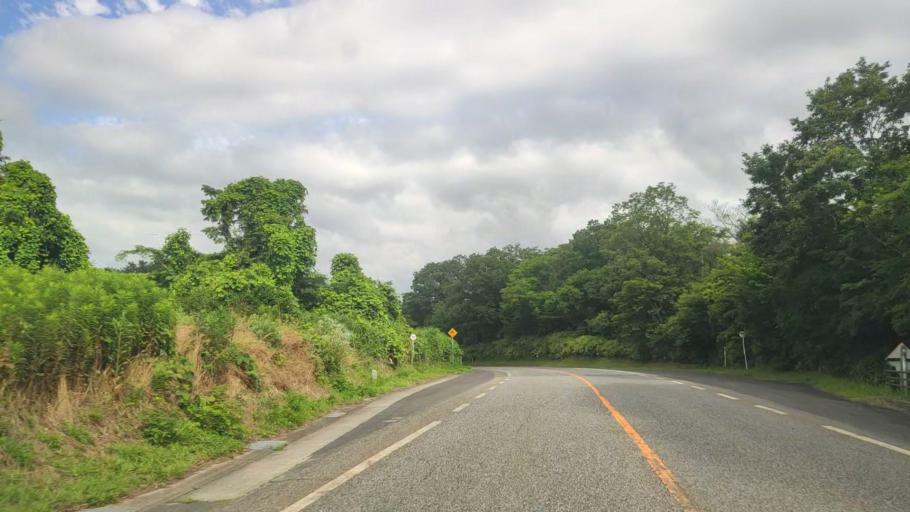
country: JP
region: Tottori
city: Yonago
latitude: 35.4142
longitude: 133.4651
